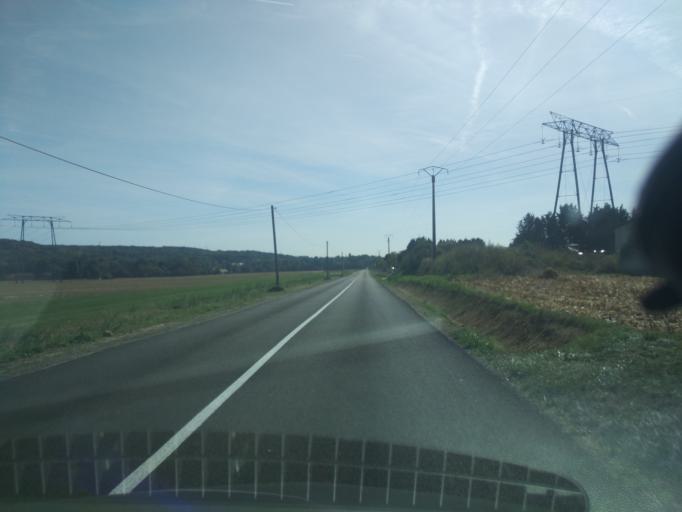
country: FR
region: Ile-de-France
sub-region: Departement de l'Essonne
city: Forges-les-Bains
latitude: 48.6370
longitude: 2.1050
